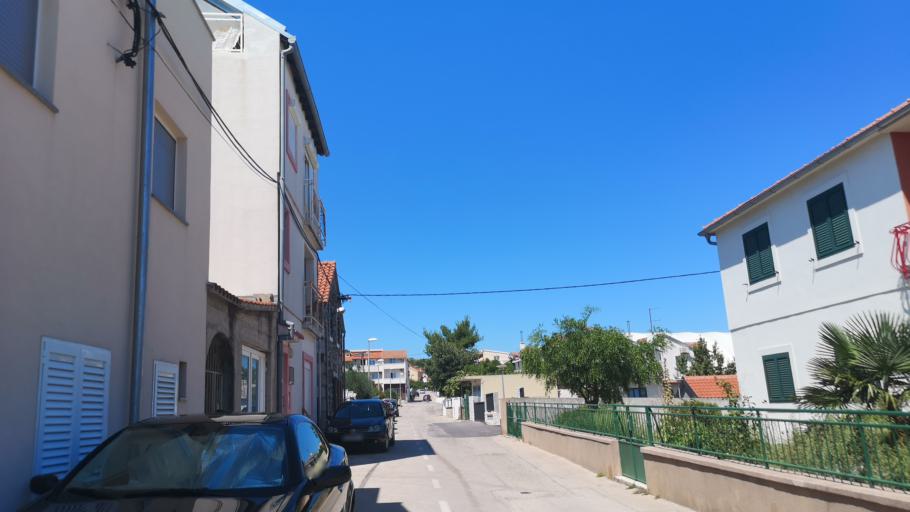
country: HR
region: Sibensko-Kniniska
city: Vodice
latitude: 43.7594
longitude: 15.7715
